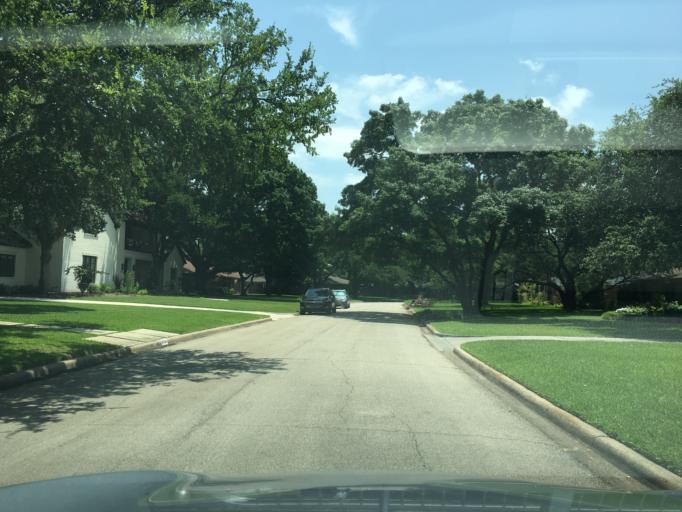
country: US
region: Texas
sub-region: Dallas County
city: Addison
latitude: 32.9117
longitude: -96.8095
